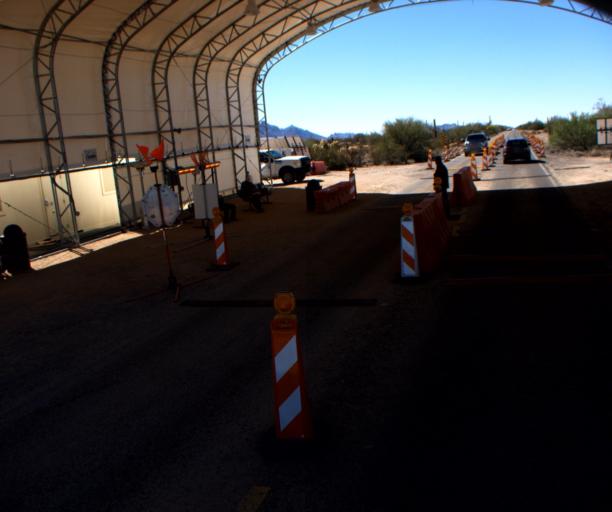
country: US
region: Arizona
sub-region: Pima County
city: Ajo
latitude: 32.2026
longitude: -112.7592
